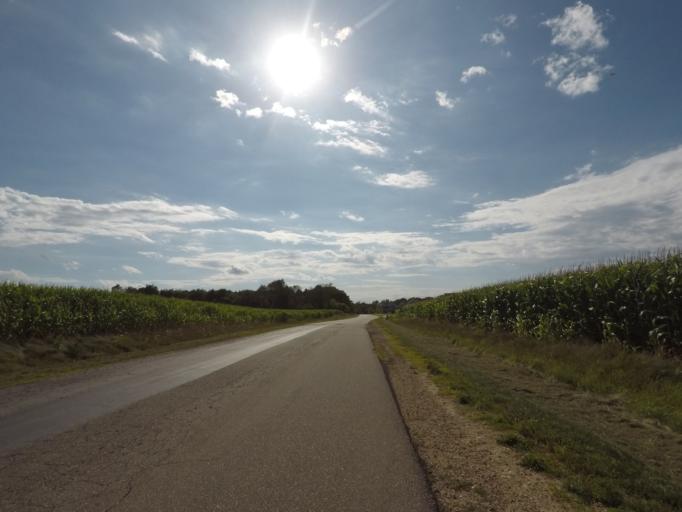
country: US
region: Wisconsin
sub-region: Dane County
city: Middleton
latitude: 43.0675
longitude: -89.5554
